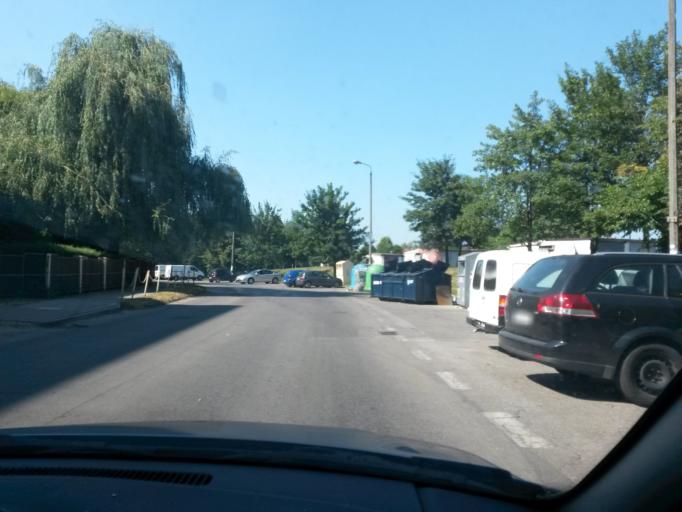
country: PL
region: Silesian Voivodeship
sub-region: Dabrowa Gornicza
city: Dabrowa Gornicza
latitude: 50.3202
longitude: 19.2067
